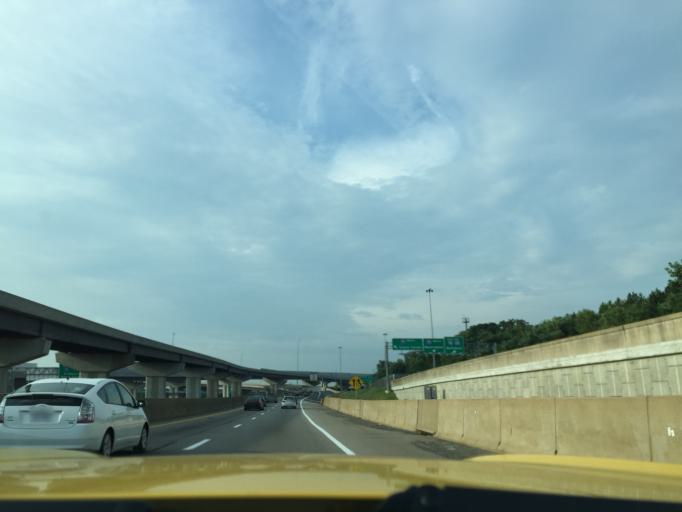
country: US
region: Virginia
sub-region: Fairfax County
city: Springfield
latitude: 38.7846
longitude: -77.1780
